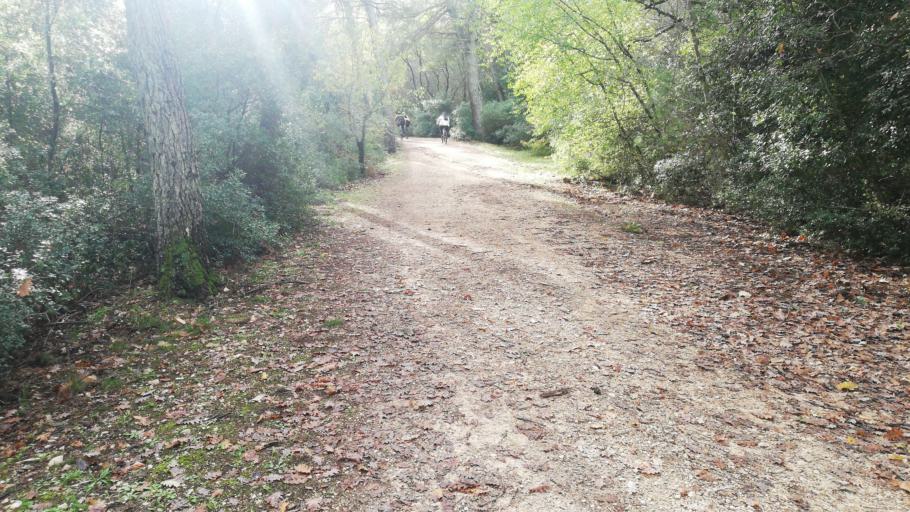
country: IT
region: Apulia
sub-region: Provincia di Bari
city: Cassano delle Murge
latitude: 40.8808
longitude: 16.7105
